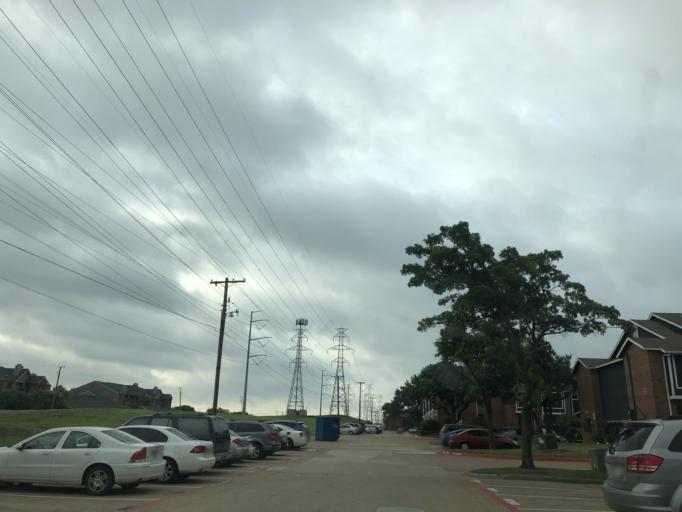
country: US
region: Texas
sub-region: Dallas County
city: Garland
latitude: 32.8398
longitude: -96.6311
